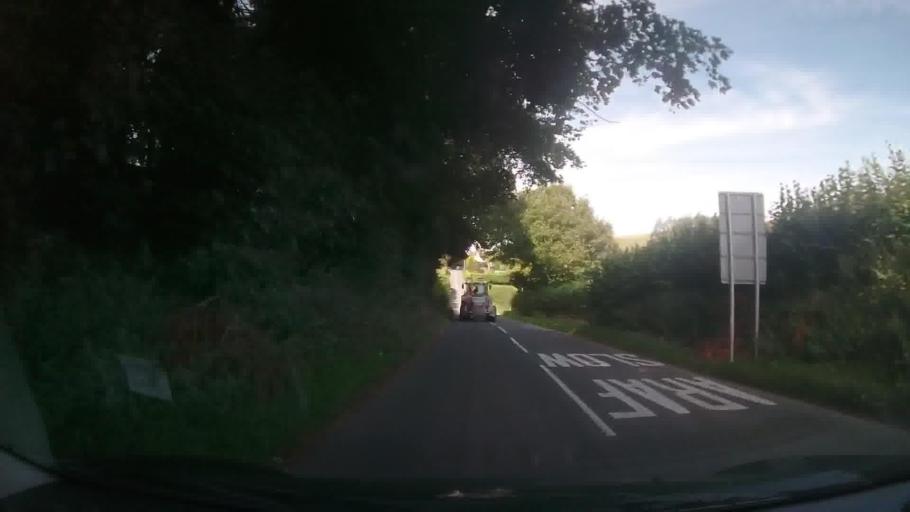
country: GB
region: Wales
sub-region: Sir Powys
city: Whitton
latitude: 52.3029
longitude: -3.0643
